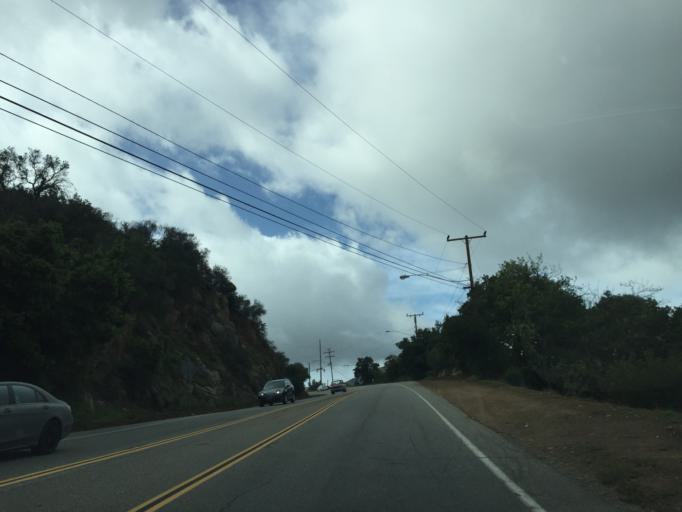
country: US
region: California
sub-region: Los Angeles County
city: Westlake Village
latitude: 34.0889
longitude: -118.8159
